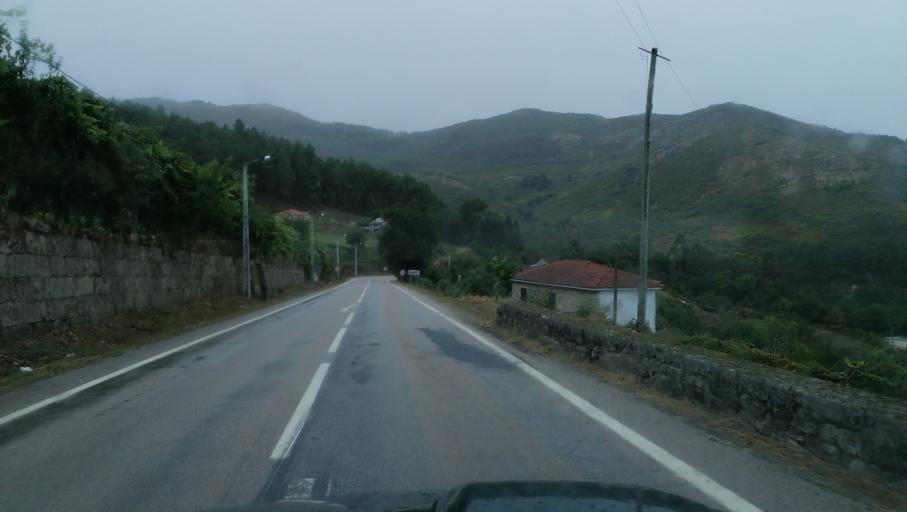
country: PT
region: Vila Real
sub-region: Ribeira de Pena
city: Ribeira de Pena
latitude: 41.5166
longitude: -7.8146
